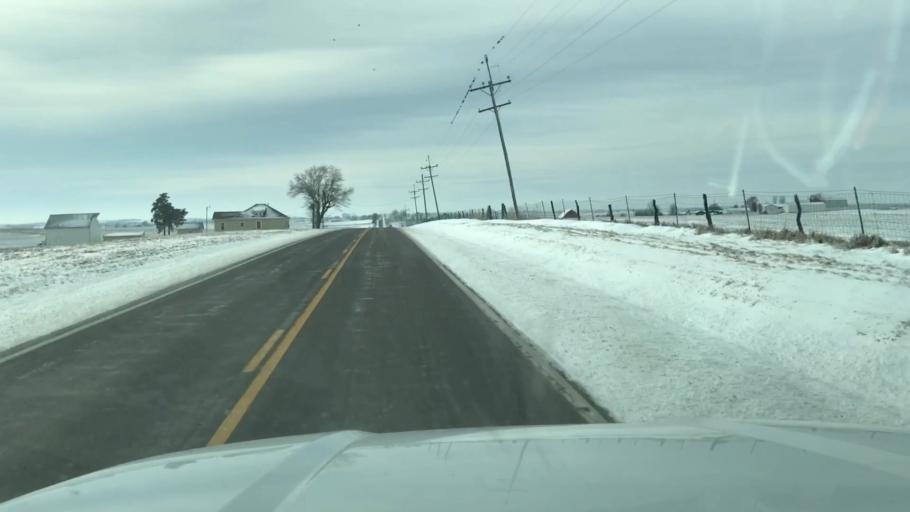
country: US
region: Missouri
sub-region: Holt County
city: Oregon
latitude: 40.0848
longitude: -95.1355
